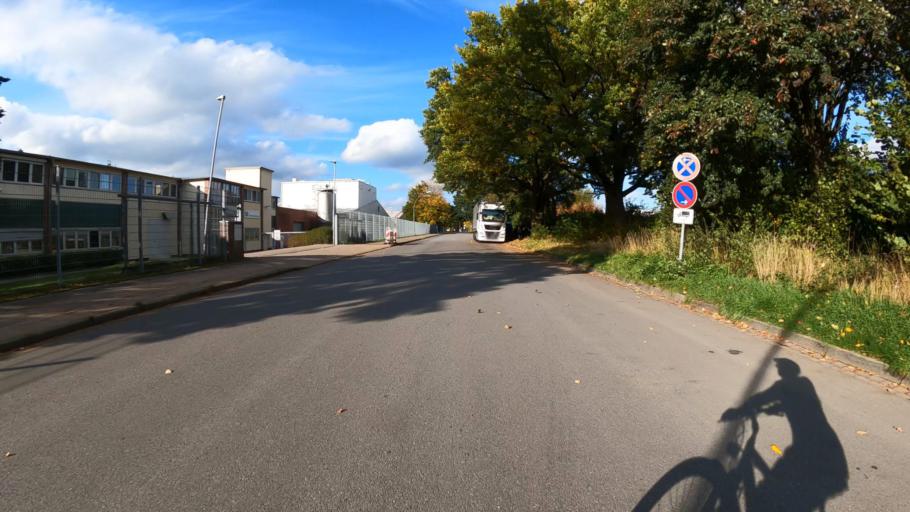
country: DE
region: Schleswig-Holstein
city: Delingsdorf
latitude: 53.6815
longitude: 10.2534
